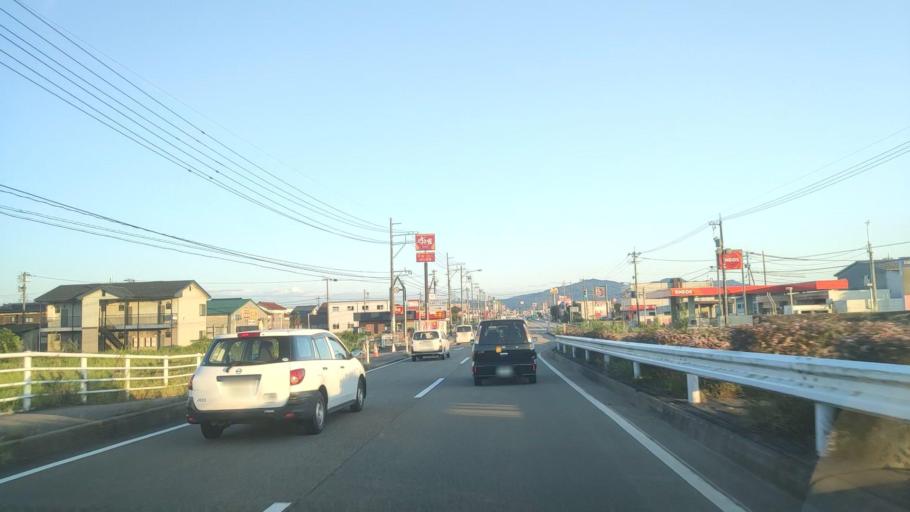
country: JP
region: Toyama
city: Himi
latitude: 36.8427
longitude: 136.9834
